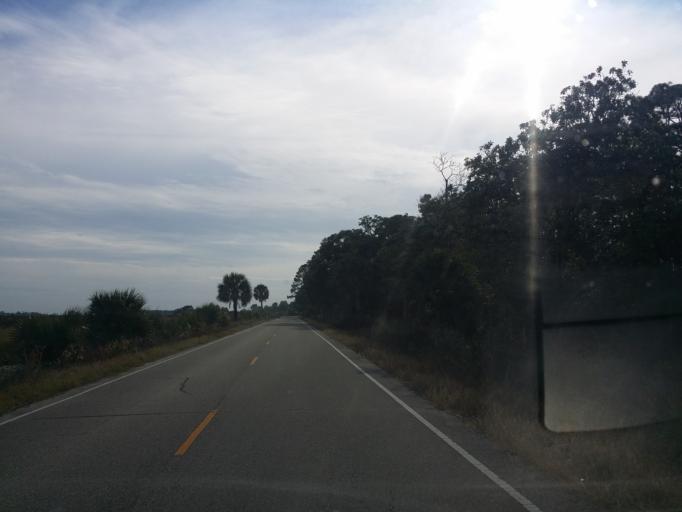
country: US
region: Florida
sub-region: Leon County
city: Woodville
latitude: 30.1143
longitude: -84.1491
